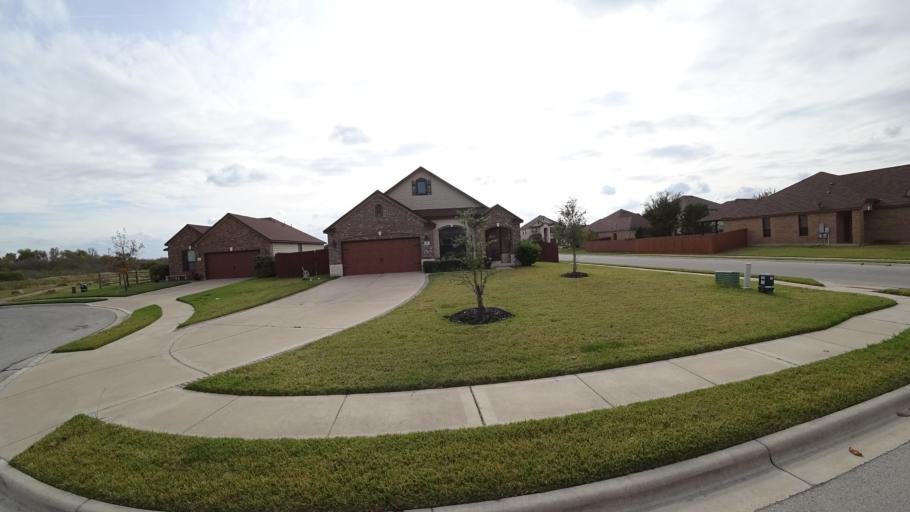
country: US
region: Texas
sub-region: Travis County
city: Wells Branch
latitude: 30.4284
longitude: -97.6593
